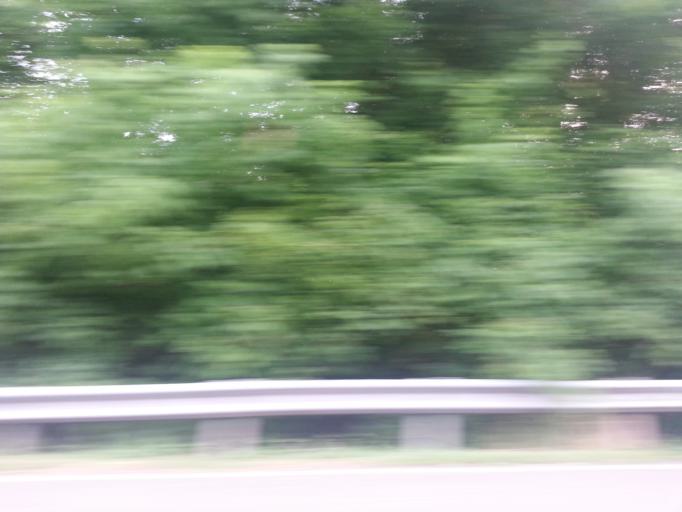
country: US
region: Tennessee
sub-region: Knox County
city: Knoxville
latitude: 35.9807
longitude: -83.8541
